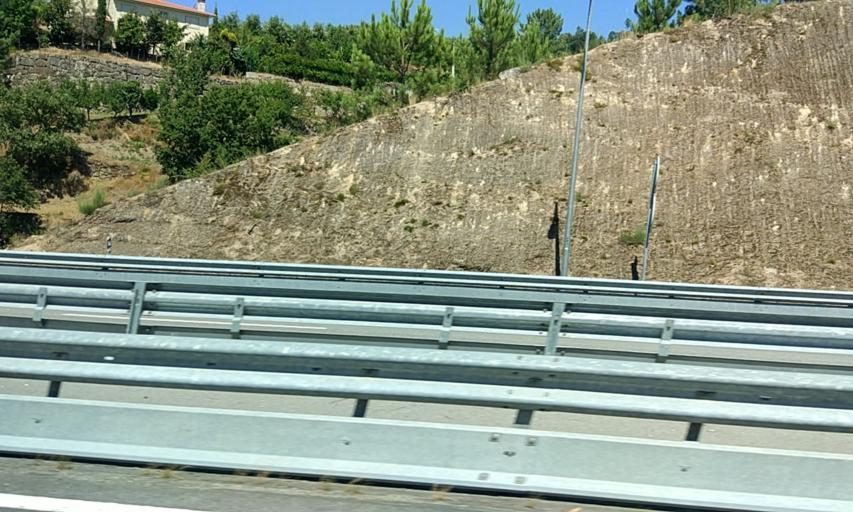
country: PT
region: Porto
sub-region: Amarante
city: Amarante
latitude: 41.2602
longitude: -8.0346
